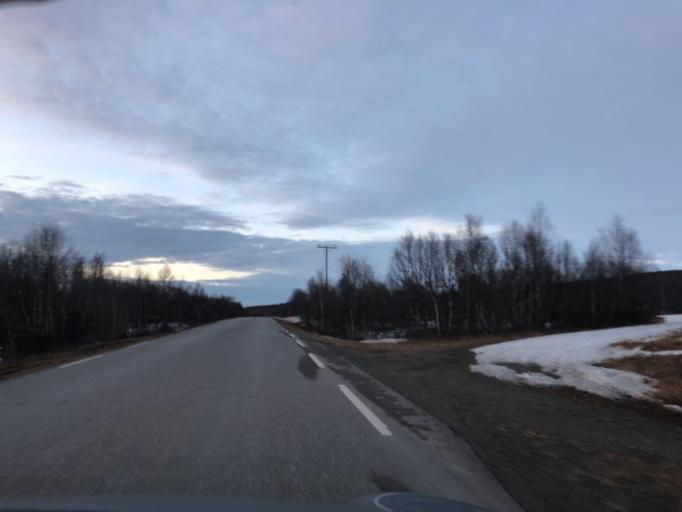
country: NO
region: Sor-Trondelag
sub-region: Tydal
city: Aas
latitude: 62.6527
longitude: 11.8660
